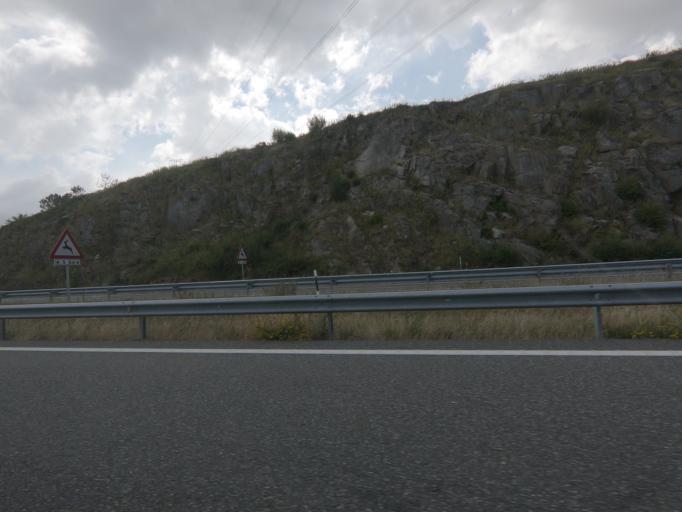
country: ES
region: Galicia
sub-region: Provincia de Ourense
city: Melon
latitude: 42.2651
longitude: -8.2107
